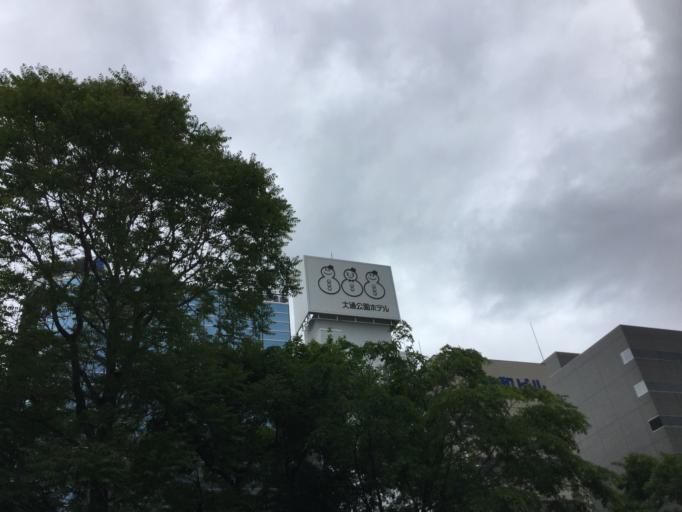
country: JP
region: Hokkaido
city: Sapporo
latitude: 43.0596
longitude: 141.3445
